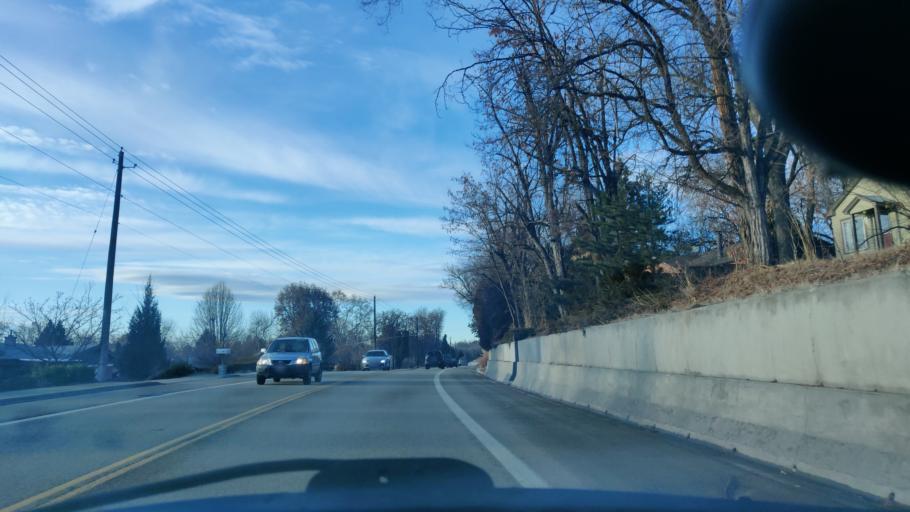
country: US
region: Idaho
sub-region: Ada County
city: Garden City
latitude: 43.6491
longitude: -116.2237
